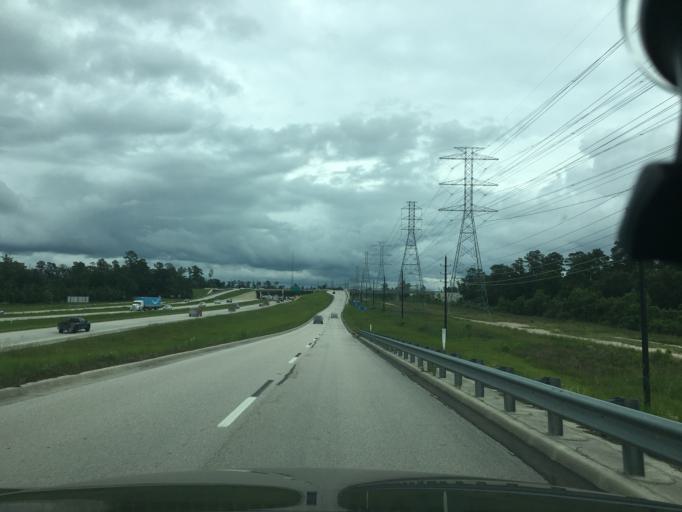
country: US
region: Texas
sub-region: Harris County
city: Spring
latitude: 30.0884
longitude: -95.4562
